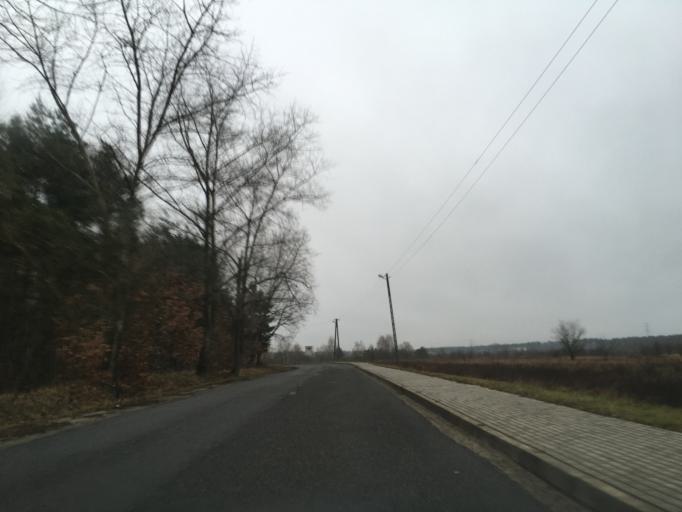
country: PL
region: Masovian Voivodeship
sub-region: Powiat piaseczynski
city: Lesznowola
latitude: 52.0700
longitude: 20.8826
